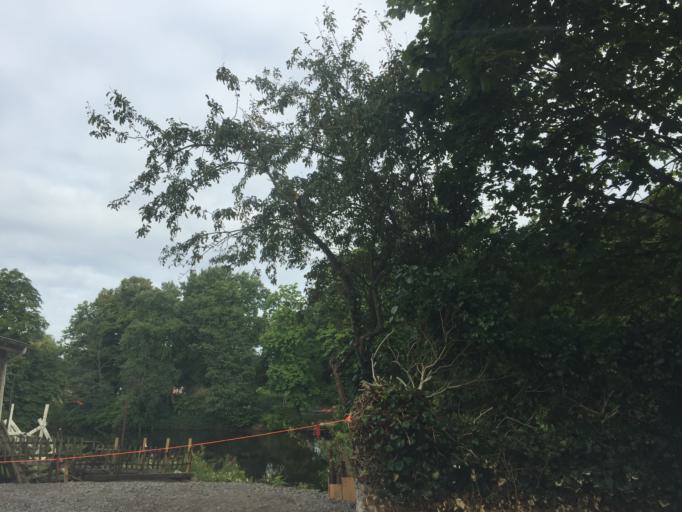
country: SE
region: Skane
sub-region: Angelholms Kommun
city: AEngelholm
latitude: 56.2447
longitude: 12.8578
